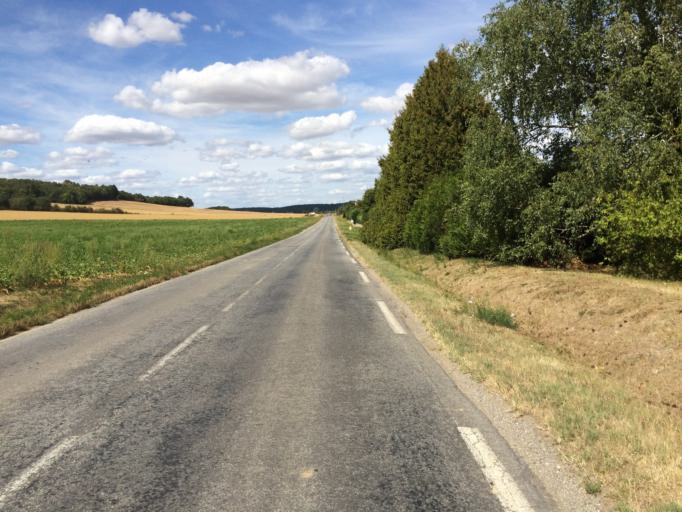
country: FR
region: Ile-de-France
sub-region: Departement de l'Essonne
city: Maisse
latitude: 48.4025
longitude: 2.3784
